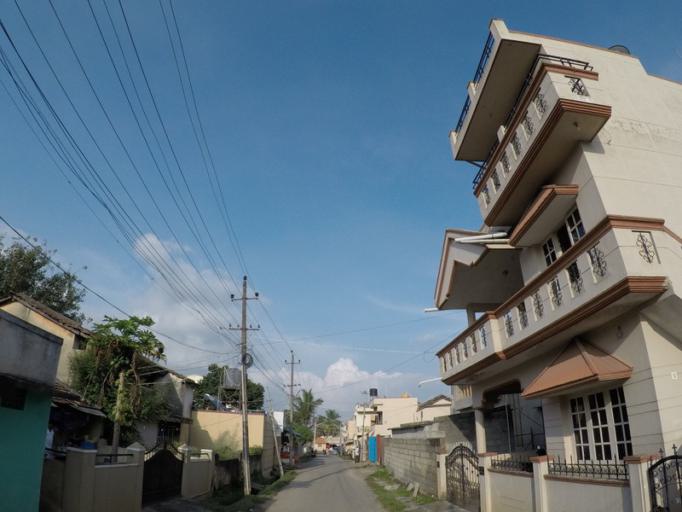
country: IN
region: Karnataka
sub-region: Chikmagalur
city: Chikmagalur
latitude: 13.3102
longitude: 75.7788
